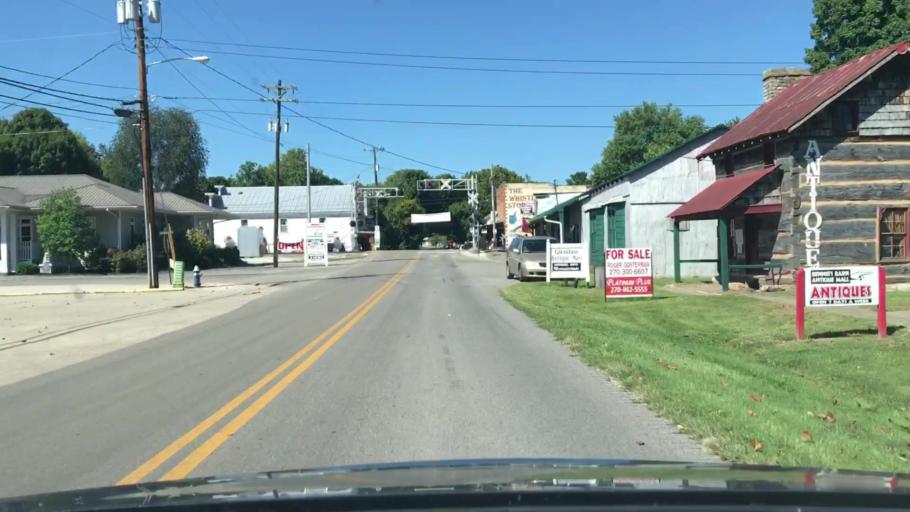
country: US
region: Kentucky
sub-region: Hardin County
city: Elizabethtown
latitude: 37.6015
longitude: -85.9041
